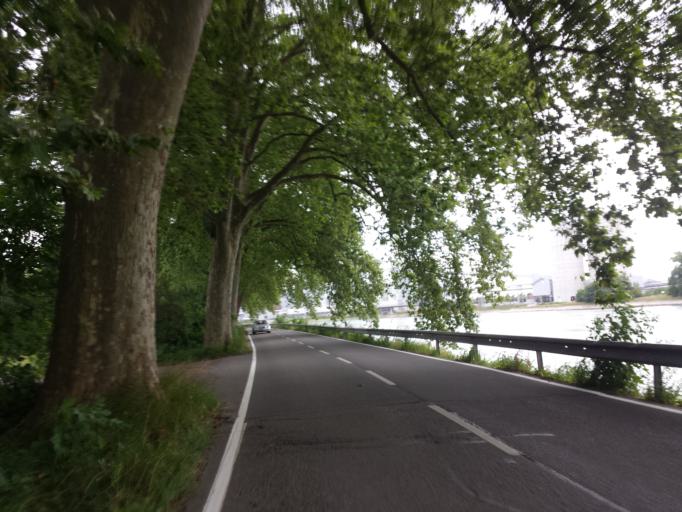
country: DE
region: Rheinland-Pfalz
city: Altrip
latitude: 49.4354
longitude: 8.5062
